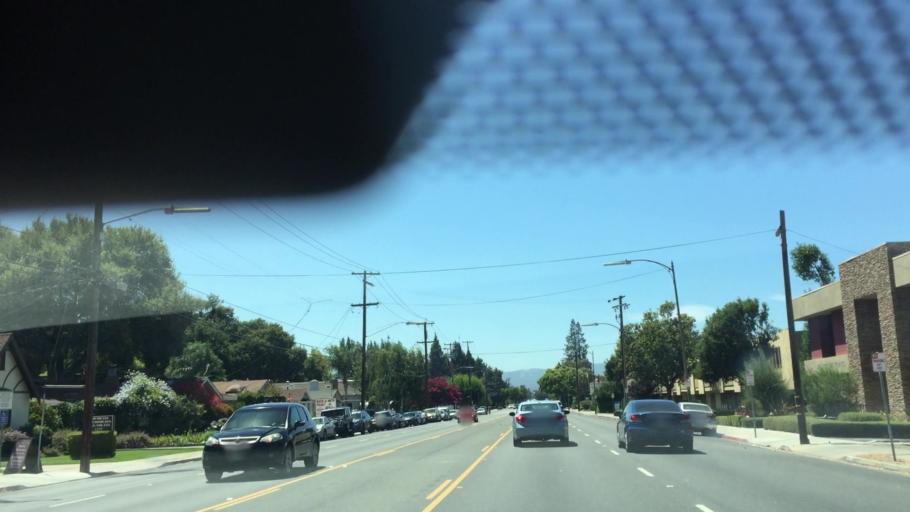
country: US
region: California
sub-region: Santa Clara County
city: Buena Vista
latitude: 37.2945
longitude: -121.9160
